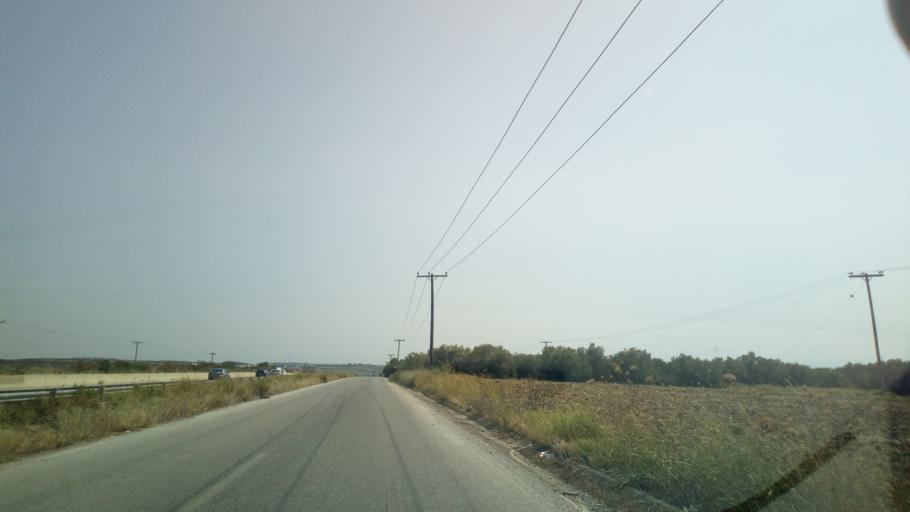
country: GR
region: Central Macedonia
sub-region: Nomos Chalkidikis
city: Lakkoma
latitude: 40.3764
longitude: 23.0420
